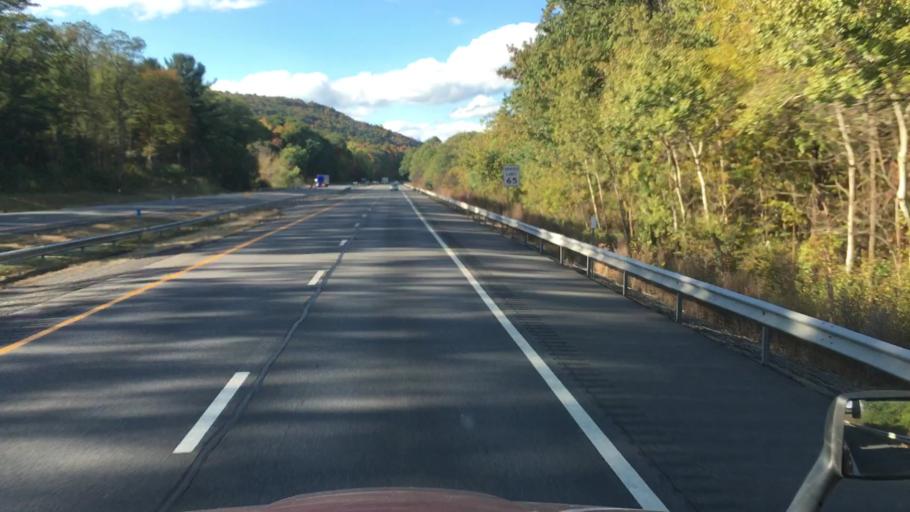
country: US
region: New York
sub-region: Schenectady County
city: Scotia
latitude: 42.8485
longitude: -74.0242
